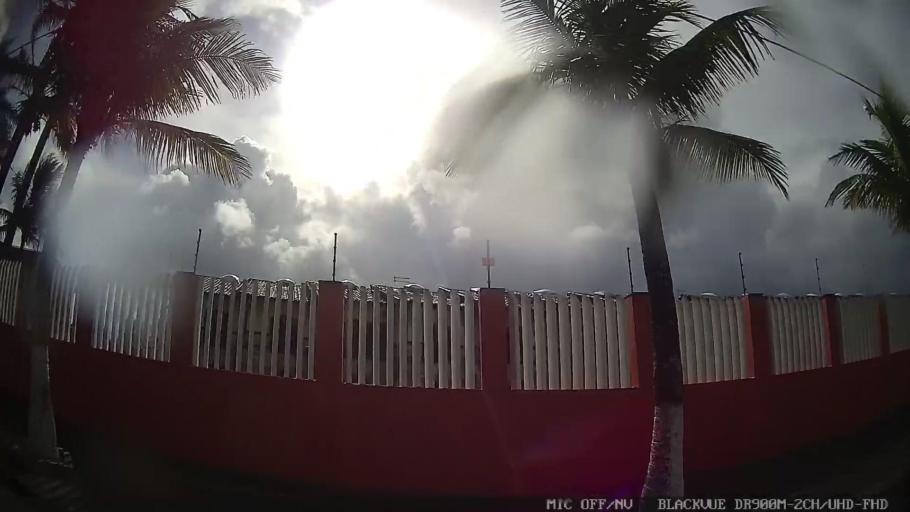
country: BR
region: Sao Paulo
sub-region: Itanhaem
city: Itanhaem
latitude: -24.2388
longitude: -46.8738
